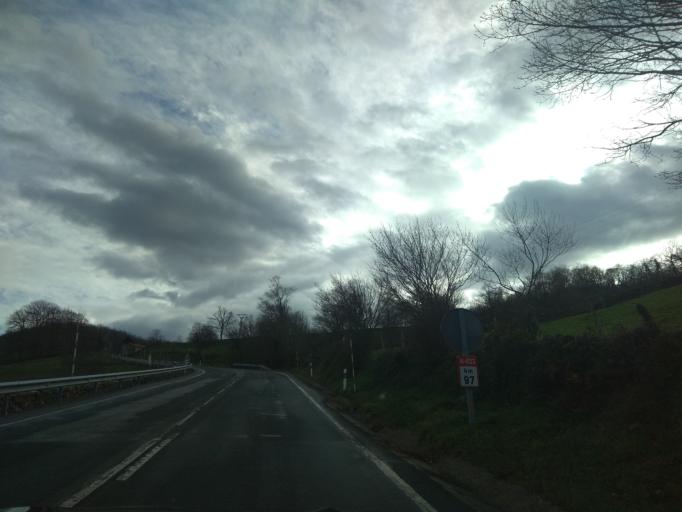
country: ES
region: Cantabria
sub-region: Provincia de Cantabria
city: San Pedro del Romeral
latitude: 43.0721
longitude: -3.8870
